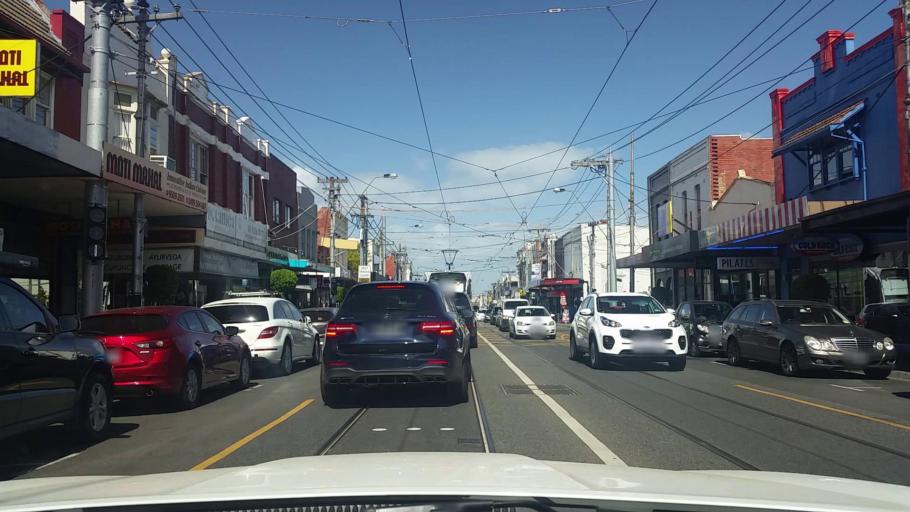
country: AU
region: Victoria
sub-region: Glen Eira
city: Caulfield North
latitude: -37.8583
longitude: 145.0290
